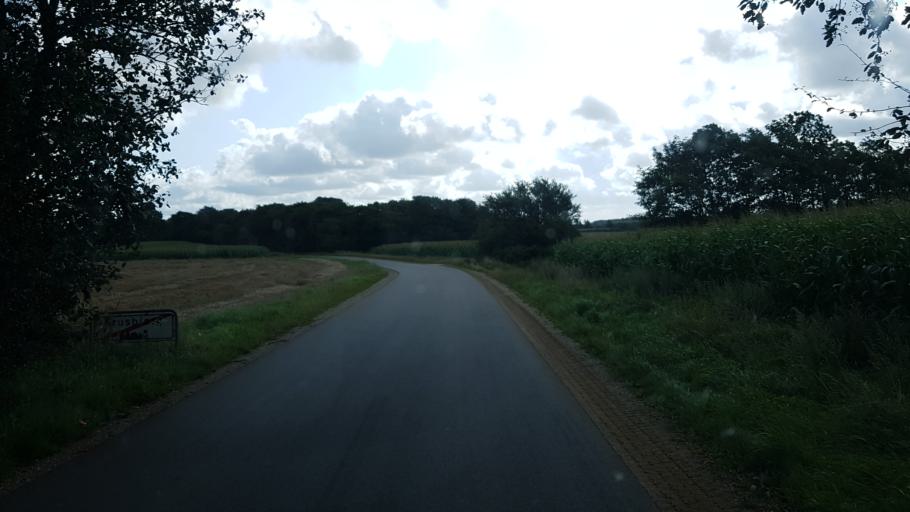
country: DK
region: South Denmark
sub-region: Varde Kommune
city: Olgod
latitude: 55.7777
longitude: 8.7074
